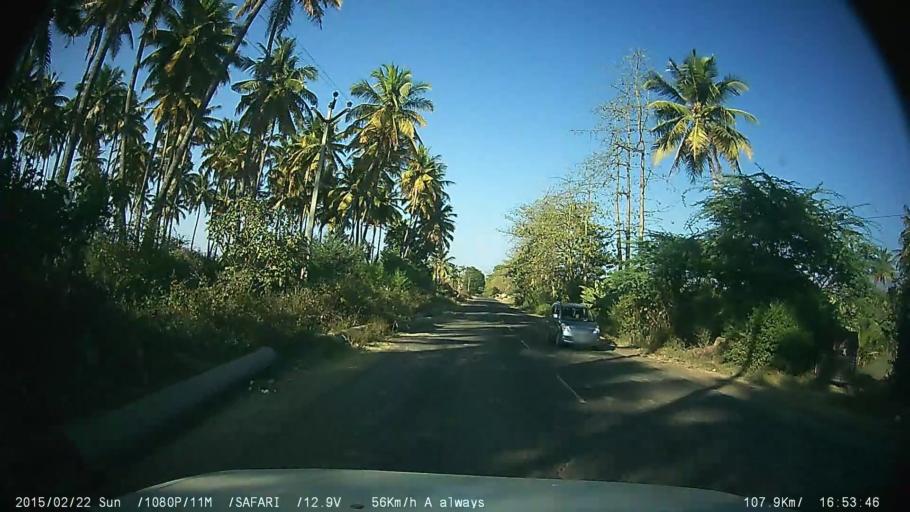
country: IN
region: Tamil Nadu
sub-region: Theni
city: Gudalur
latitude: 9.6667
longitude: 77.2328
